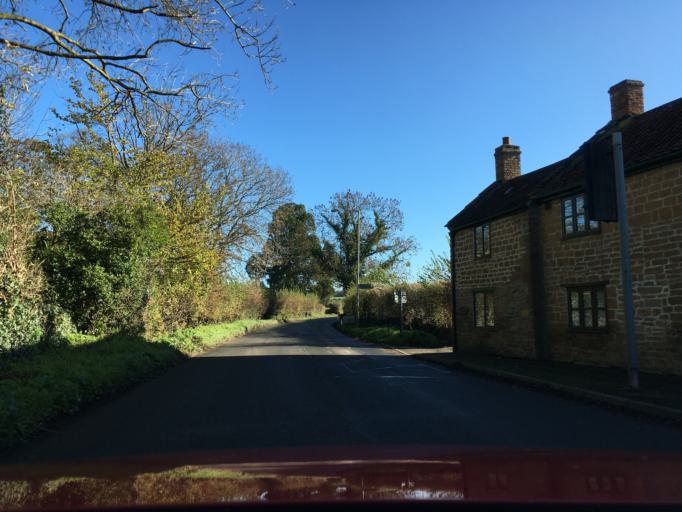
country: GB
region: England
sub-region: Somerset
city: Martock
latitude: 50.9843
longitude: -2.7659
